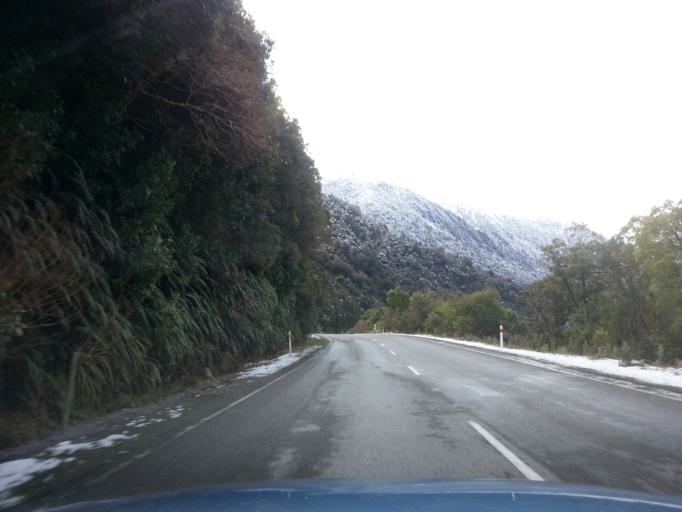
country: NZ
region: West Coast
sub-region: Grey District
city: Greymouth
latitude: -42.8131
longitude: 171.5655
